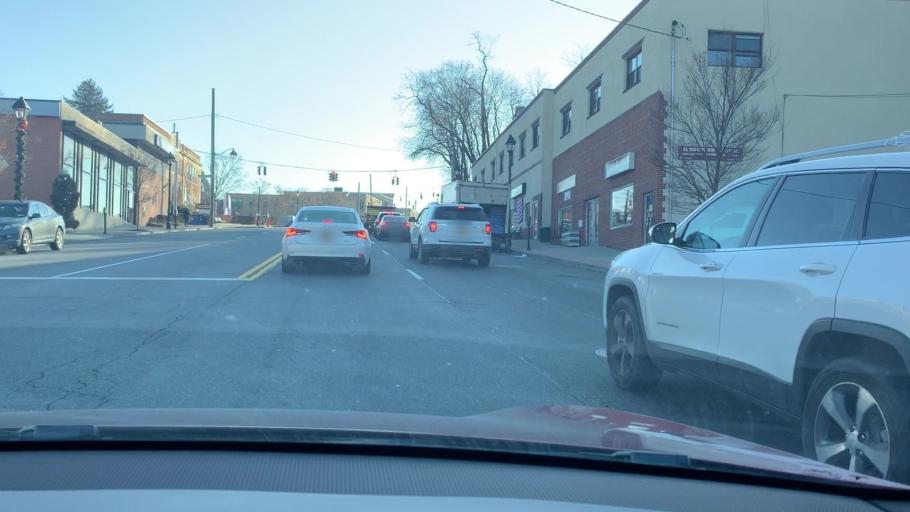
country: US
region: New York
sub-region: Westchester County
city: Elmsford
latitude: 41.0543
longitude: -73.8182
